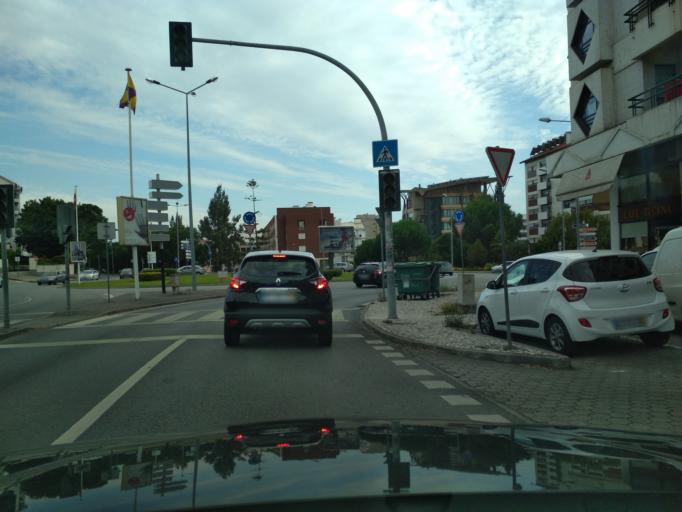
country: PT
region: Coimbra
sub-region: Coimbra
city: Coimbra
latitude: 40.2054
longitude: -8.4011
